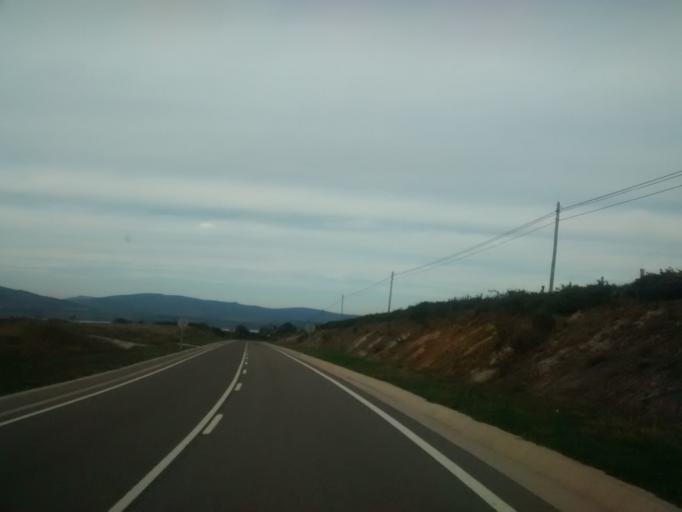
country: ES
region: Castille and Leon
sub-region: Provincia de Burgos
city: Arija
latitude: 42.9775
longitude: -3.9958
